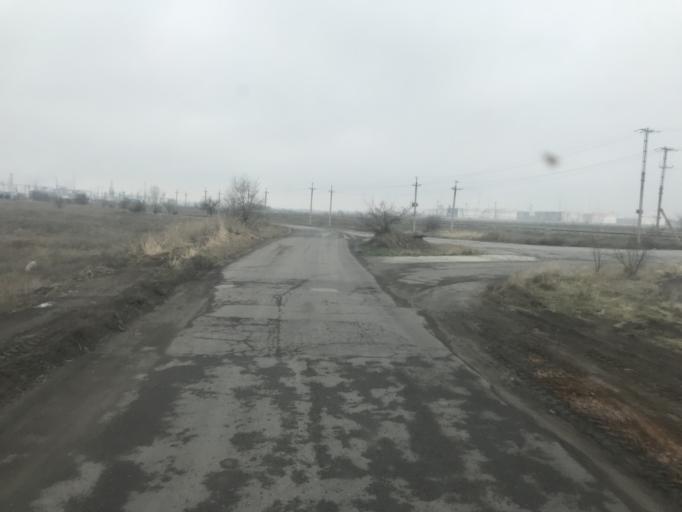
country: RU
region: Volgograd
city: Svetlyy Yar
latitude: 48.4924
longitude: 44.6577
